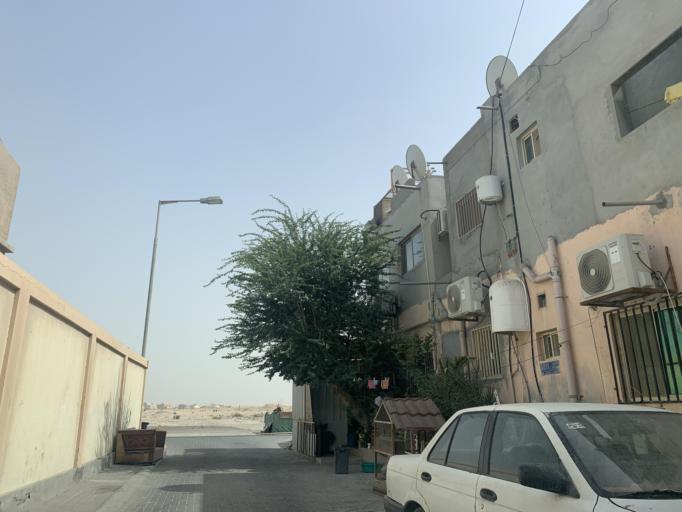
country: BH
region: Northern
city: Madinat `Isa
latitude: 26.1561
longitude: 50.5132
